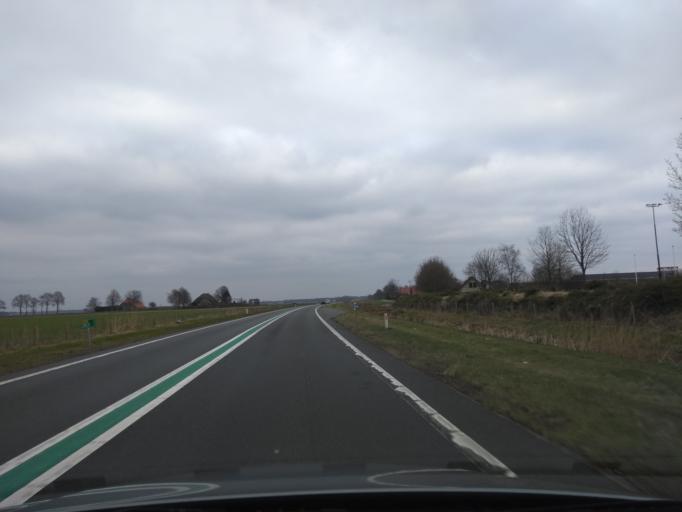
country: NL
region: Overijssel
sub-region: Gemeente Twenterand
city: Den Ham
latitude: 52.5573
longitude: 6.4731
